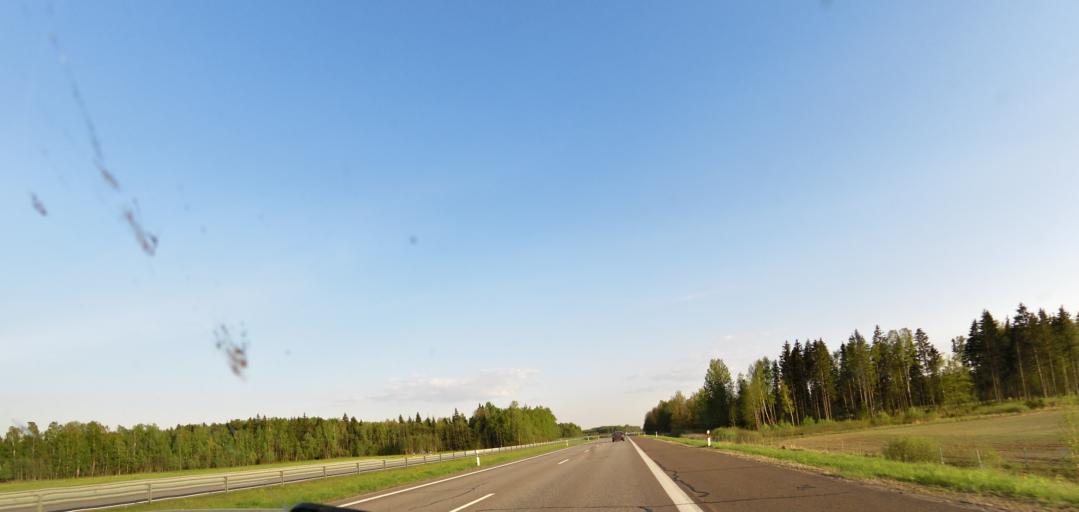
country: LT
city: Sirvintos
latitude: 55.0565
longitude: 24.8897
